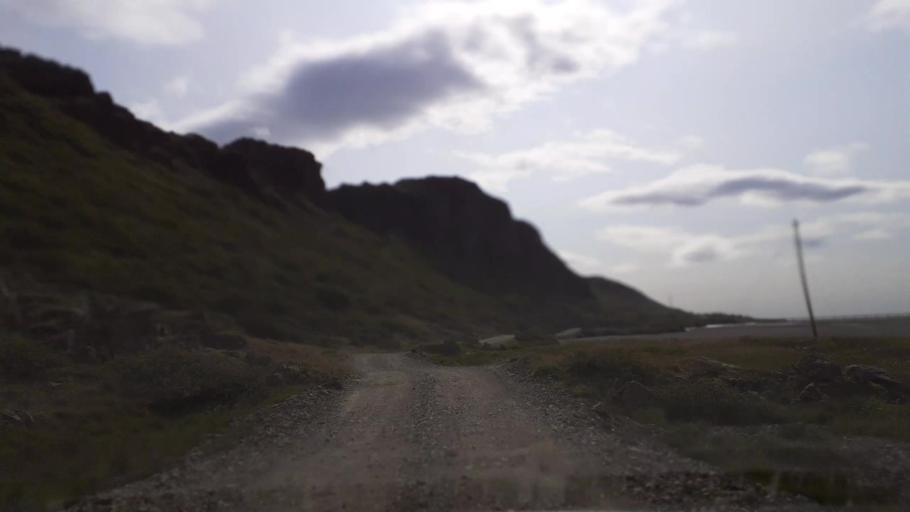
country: IS
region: East
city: Hoefn
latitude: 64.4335
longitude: -14.8940
